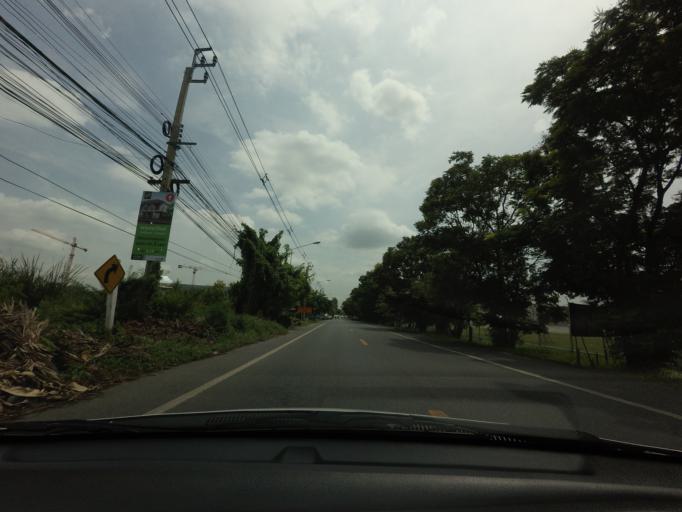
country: TH
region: Bangkok
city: Khan Na Yao
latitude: 13.8596
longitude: 100.6765
